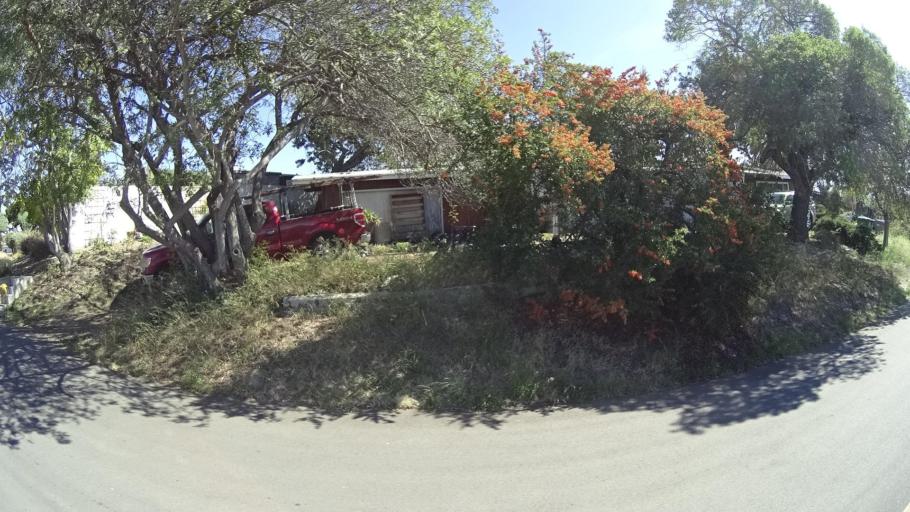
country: US
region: California
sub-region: San Diego County
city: Casa de Oro-Mount Helix
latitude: 32.7519
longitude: -116.9715
